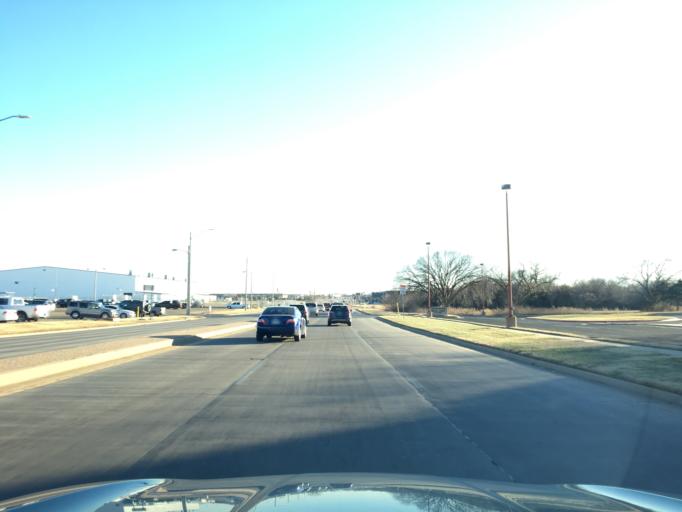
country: US
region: Kansas
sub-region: Sedgwick County
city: Bellaire
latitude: 37.6865
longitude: -97.2263
